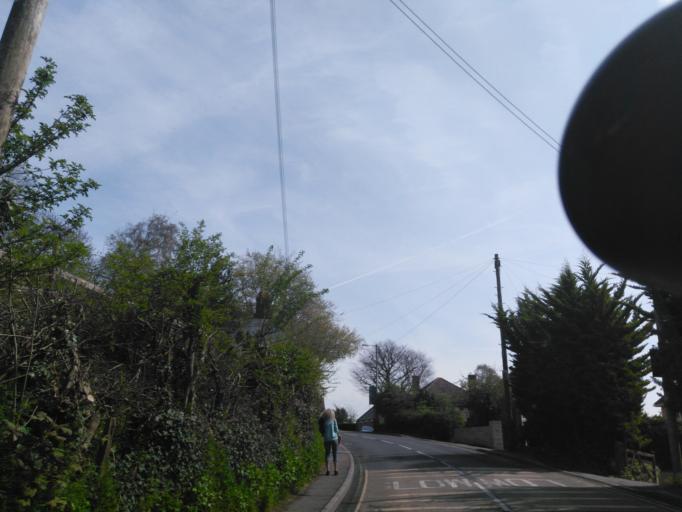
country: GB
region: England
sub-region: Somerset
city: Glastonbury
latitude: 51.1428
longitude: -2.7059
